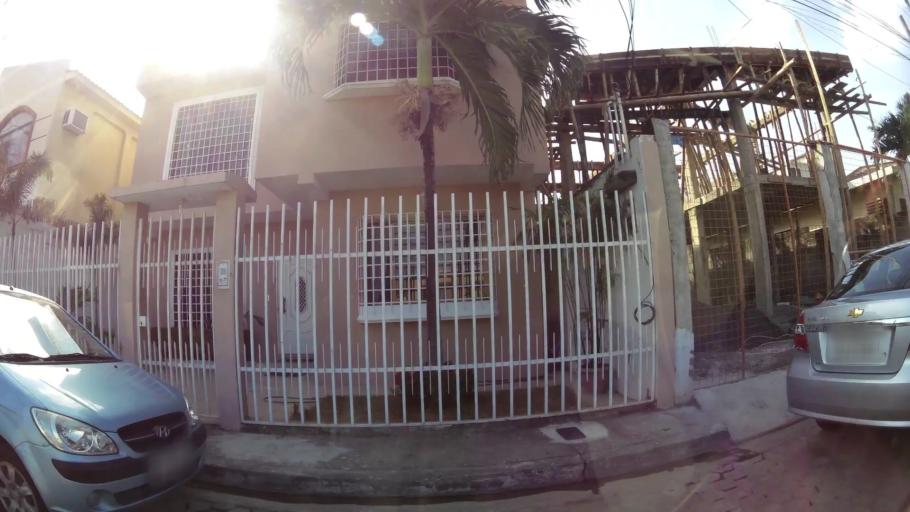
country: EC
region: Guayas
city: Santa Lucia
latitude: -2.1584
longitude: -79.9455
